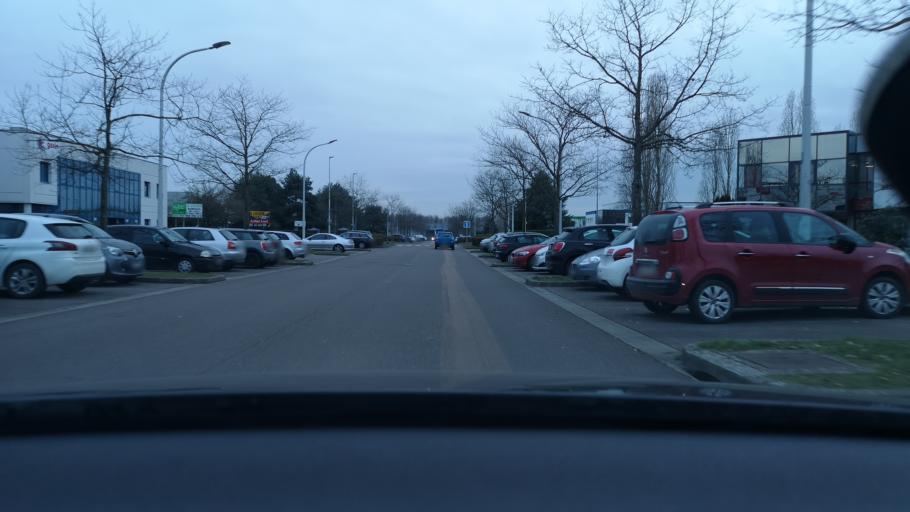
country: FR
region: Bourgogne
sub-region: Departement de Saone-et-Loire
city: Chalon-sur-Saone
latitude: 46.7676
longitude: 4.8583
